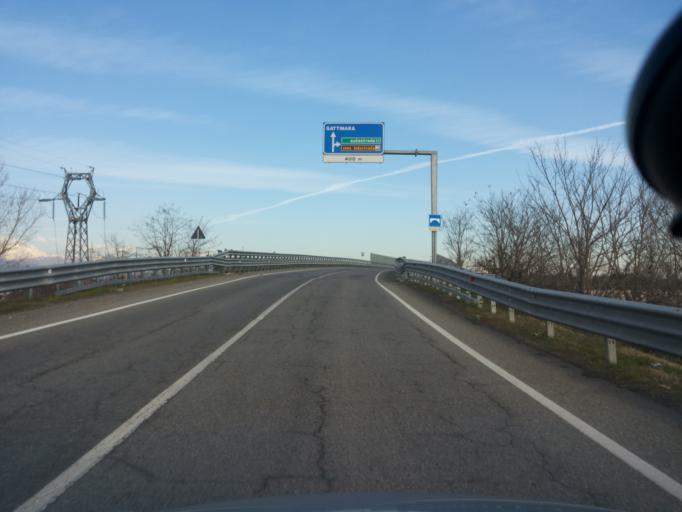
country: IT
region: Piedmont
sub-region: Provincia di Vercelli
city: Greggio
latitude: 45.4600
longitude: 8.3853
